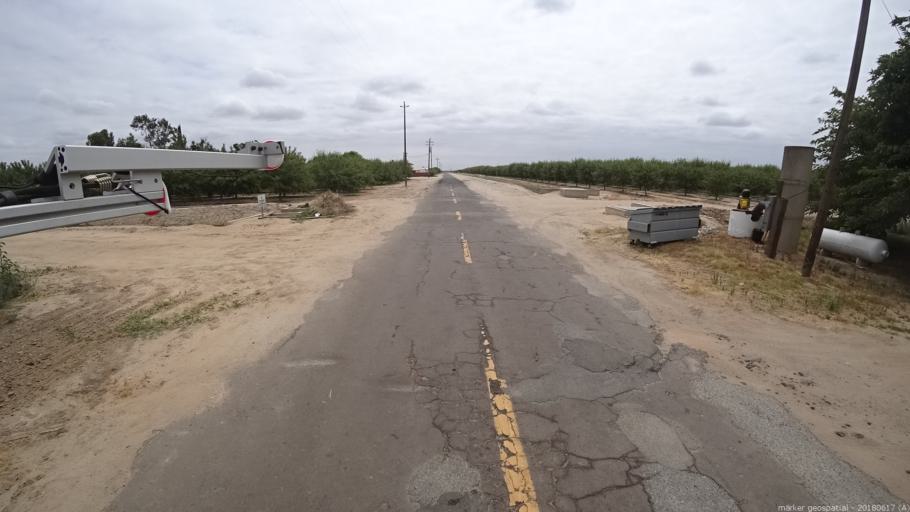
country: US
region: California
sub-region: Madera County
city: Fairmead
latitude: 37.0038
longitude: -120.1979
